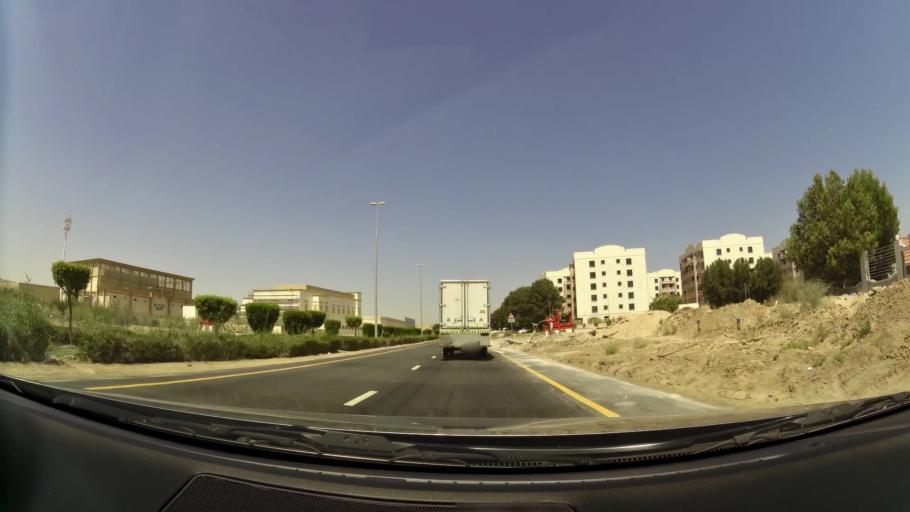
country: AE
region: Dubai
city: Dubai
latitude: 24.9851
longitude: 55.2050
